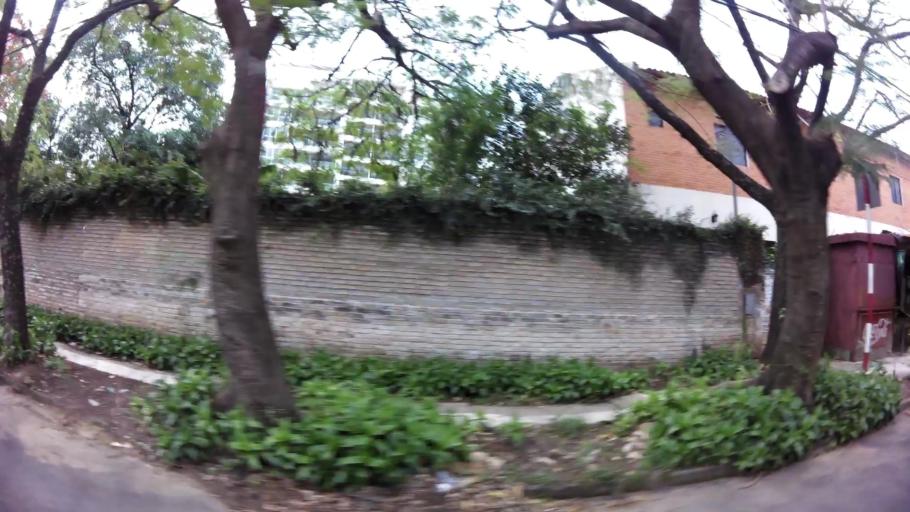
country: PY
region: Asuncion
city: Asuncion
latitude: -25.2882
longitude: -57.5872
